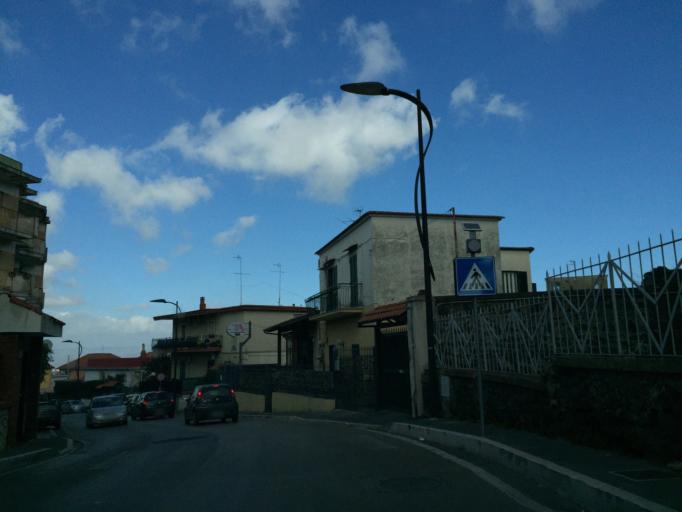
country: IT
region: Campania
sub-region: Provincia di Napoli
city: Massa di Somma
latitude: 40.8458
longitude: 14.3730
